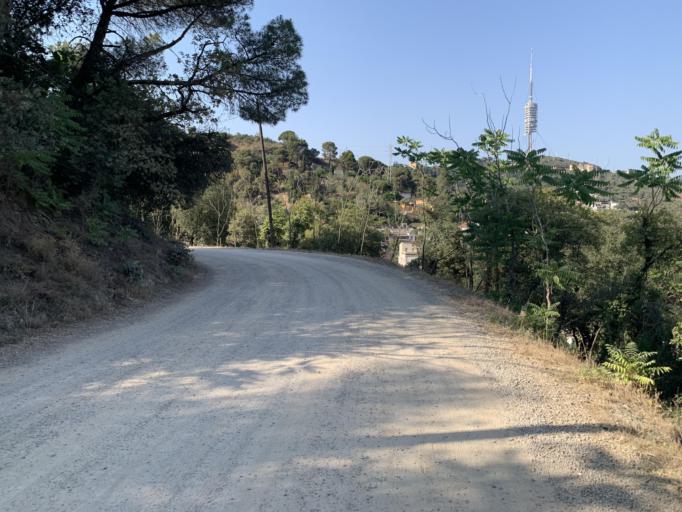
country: ES
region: Catalonia
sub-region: Provincia de Barcelona
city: les Corts
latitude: 41.4071
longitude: 2.1047
